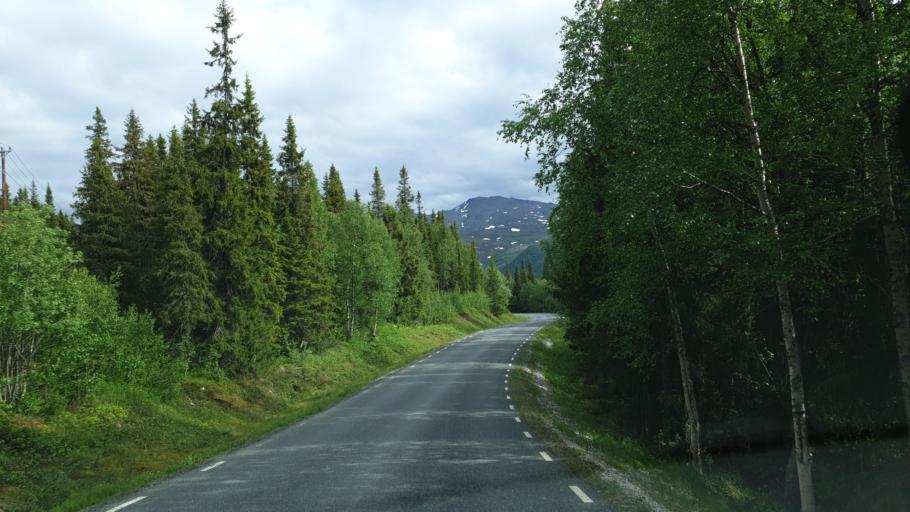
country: SE
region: Vaesterbotten
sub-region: Vilhelmina Kommun
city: Sjoberg
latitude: 65.2636
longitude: 15.3779
